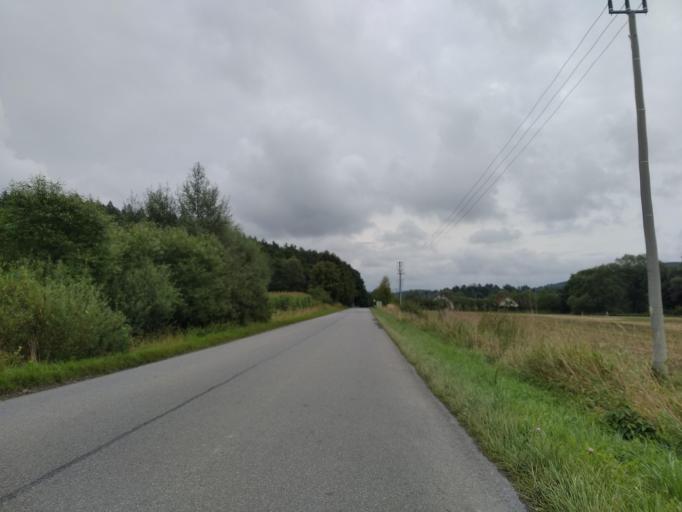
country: PL
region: Subcarpathian Voivodeship
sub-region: Powiat przemyski
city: Bircza
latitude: 49.6891
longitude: 22.3956
